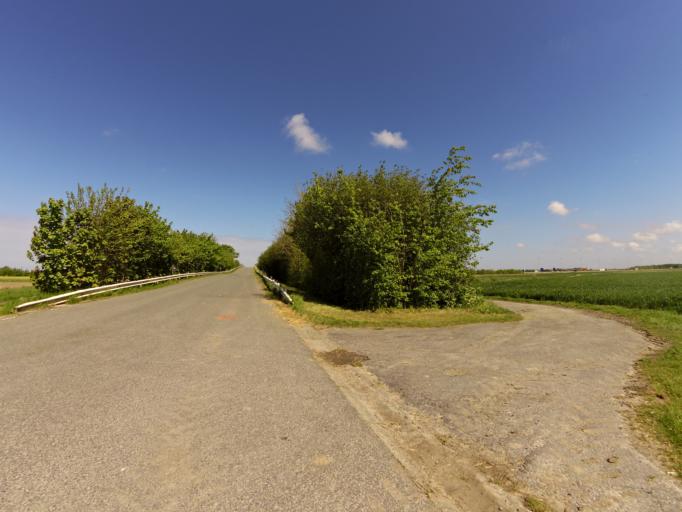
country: BE
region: Flanders
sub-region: Provincie West-Vlaanderen
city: Middelkerke
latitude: 51.1359
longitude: 2.8439
